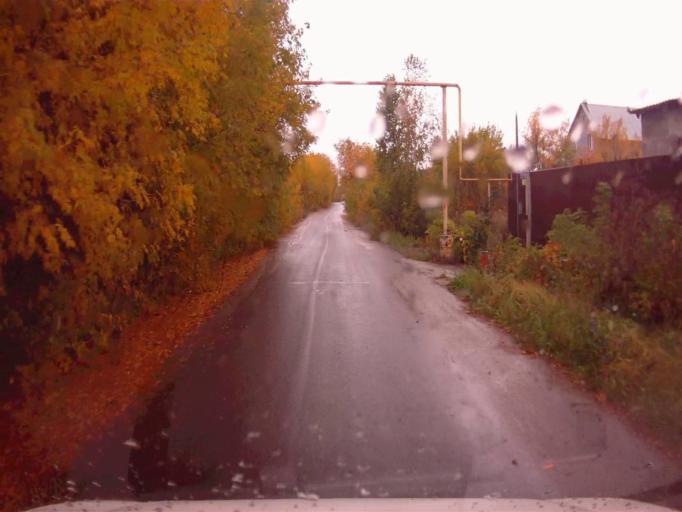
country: RU
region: Chelyabinsk
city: Dolgoderevenskoye
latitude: 55.3033
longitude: 61.3374
